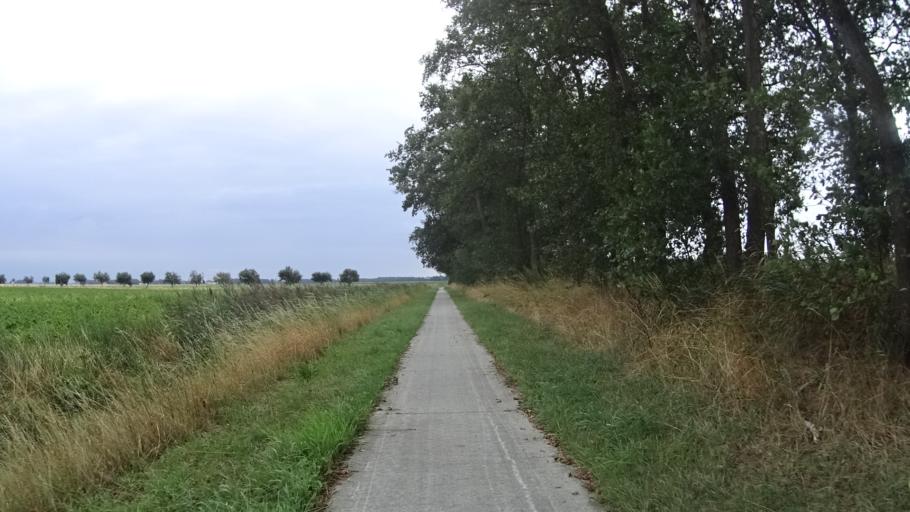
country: NL
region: Groningen
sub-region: Gemeente Slochteren
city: Slochteren
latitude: 53.2070
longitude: 6.8344
